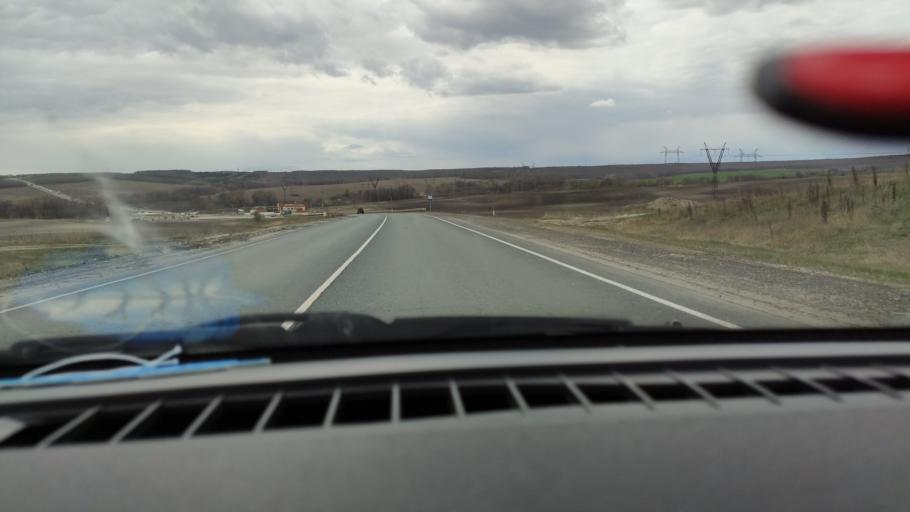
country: RU
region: Saratov
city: Sinodskoye
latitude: 51.9226
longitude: 46.5623
